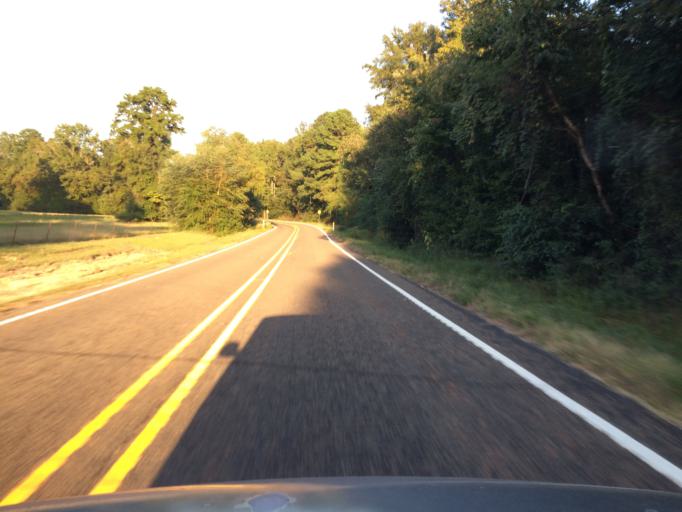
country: US
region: Texas
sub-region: Wood County
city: Quitman
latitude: 32.7360
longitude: -95.3036
